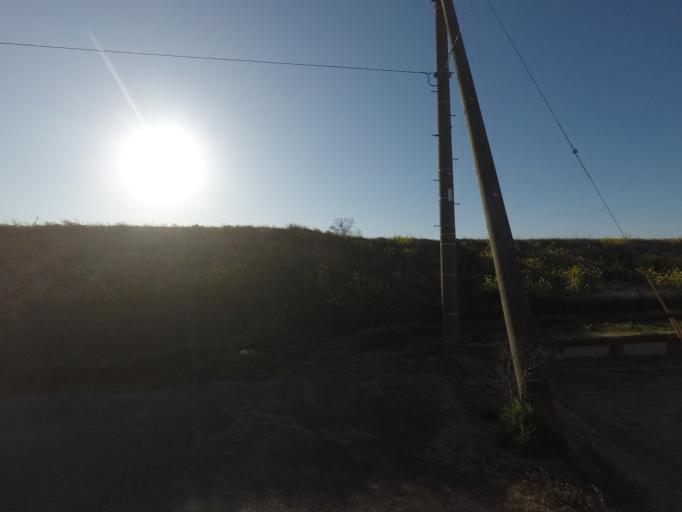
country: JP
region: Ibaraki
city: Ishige
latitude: 36.1652
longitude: 140.0080
